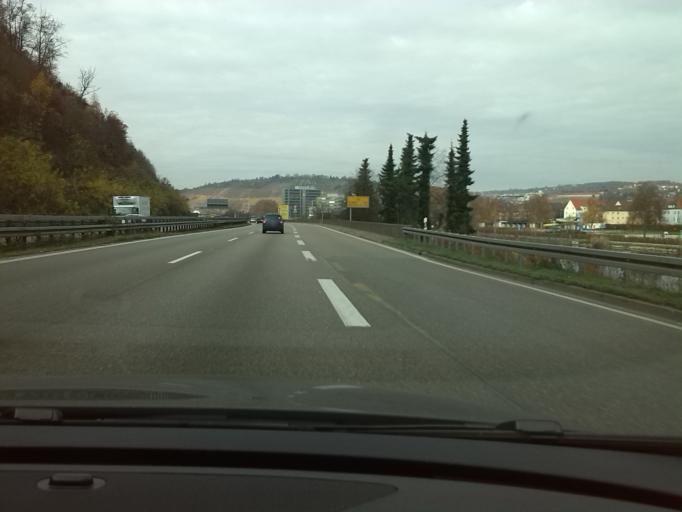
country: DE
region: Baden-Wuerttemberg
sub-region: Regierungsbezirk Stuttgart
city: Esslingen
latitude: 48.7286
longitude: 9.3172
